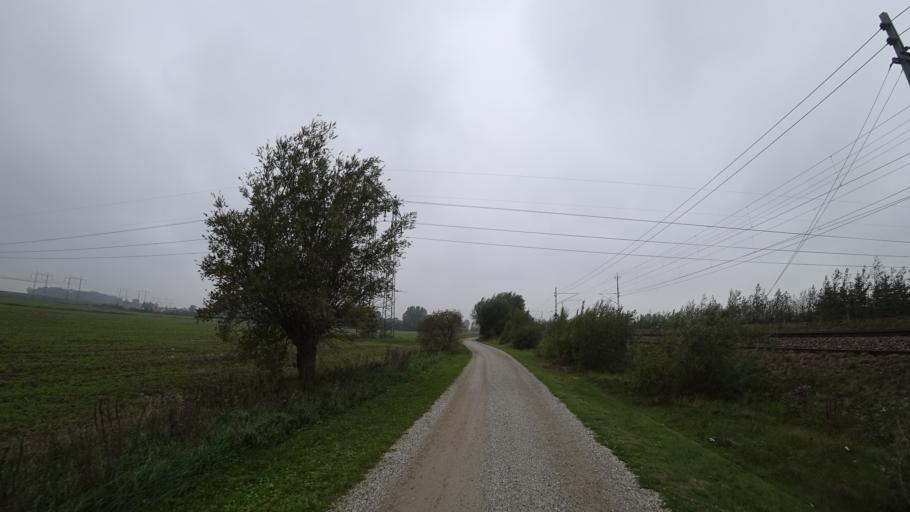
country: SE
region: Skane
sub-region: Kavlinge Kommun
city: Kaevlinge
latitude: 55.8174
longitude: 13.0779
